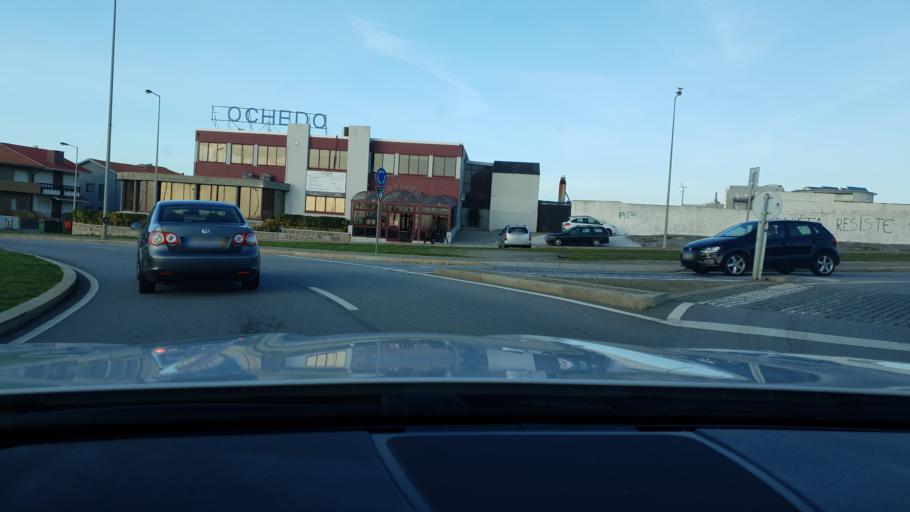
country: PT
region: Porto
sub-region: Matosinhos
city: Santa Cruz do Bispo
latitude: 41.2196
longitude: -8.7122
